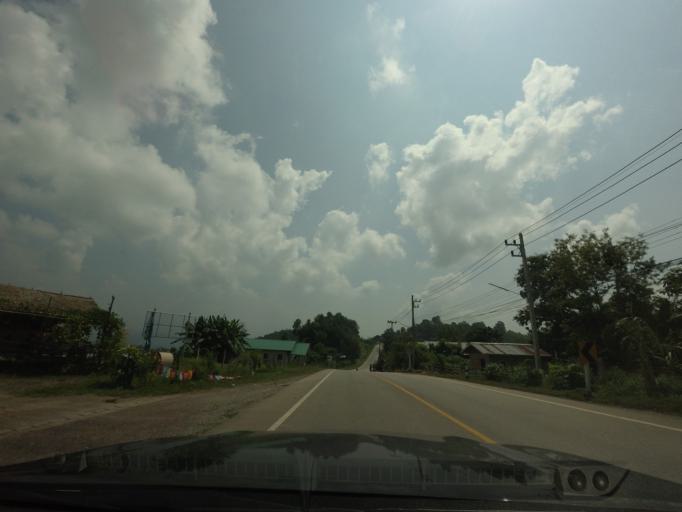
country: TH
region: Nan
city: Santi Suk
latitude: 18.9165
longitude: 100.8781
